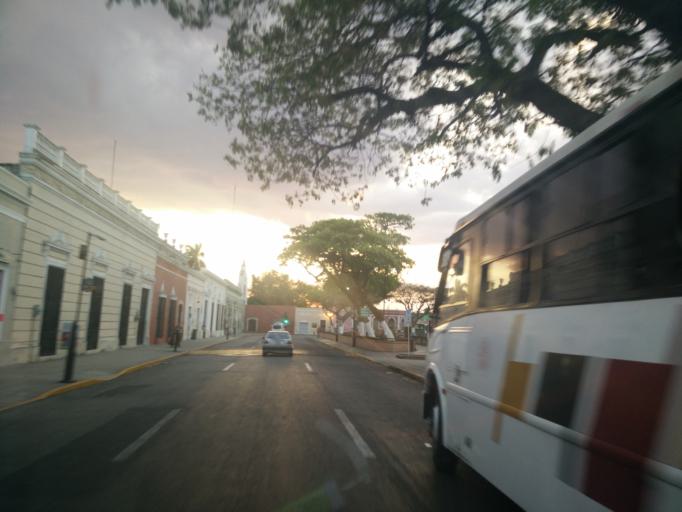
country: MX
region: Yucatan
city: Merida
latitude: 20.9623
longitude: -89.6258
